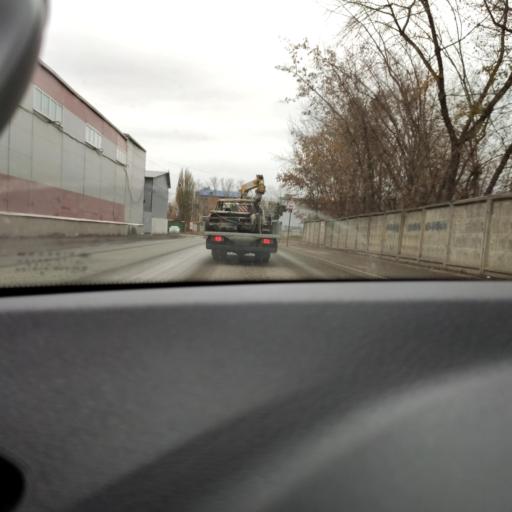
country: RU
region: Samara
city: Smyshlyayevka
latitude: 53.2093
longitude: 50.3005
